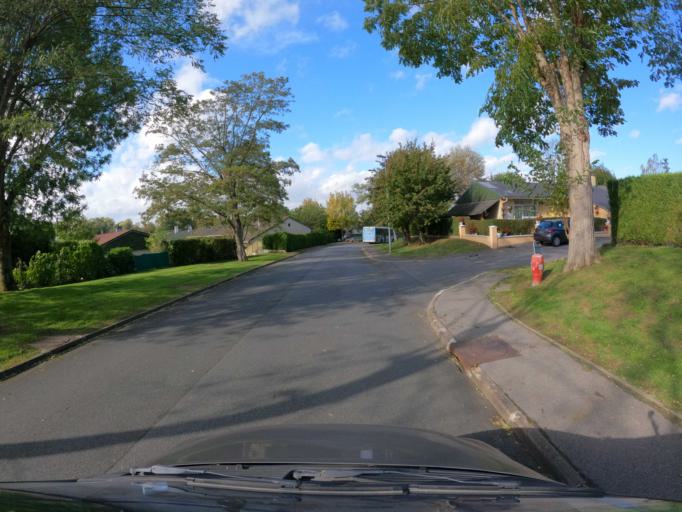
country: FR
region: Ile-de-France
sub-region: Departement de Seine-et-Marne
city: Coupvray
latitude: 48.8916
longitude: 2.8102
